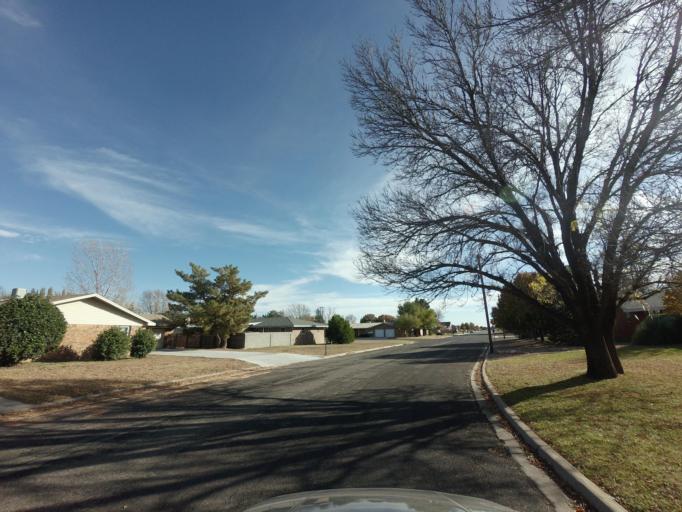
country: US
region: New Mexico
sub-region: Curry County
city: Clovis
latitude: 34.4179
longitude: -103.1744
